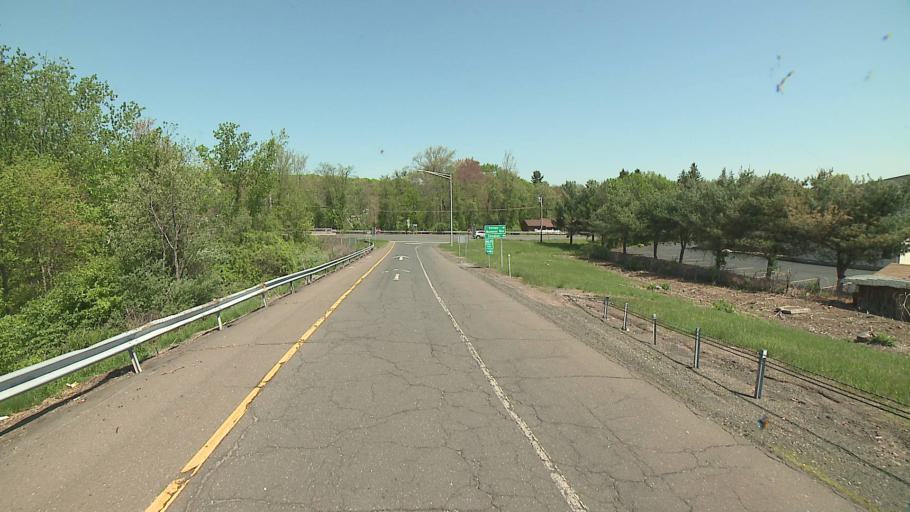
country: US
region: Connecticut
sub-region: Hartford County
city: Manchester
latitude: 41.8241
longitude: -72.5018
